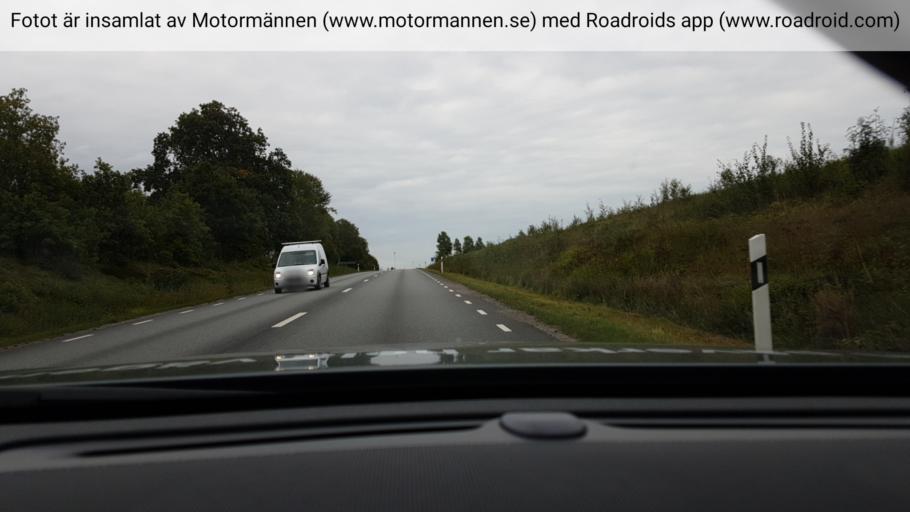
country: SE
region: Joenkoeping
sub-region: Gislaveds Kommun
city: Smalandsstenar
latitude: 57.1633
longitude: 13.4349
